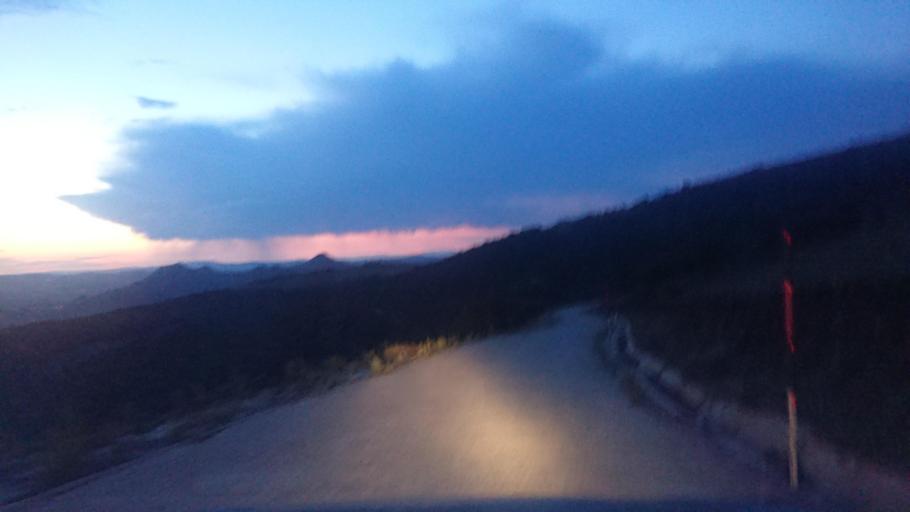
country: TR
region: Aksaray
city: Ortakoy
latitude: 38.6409
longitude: 34.0248
